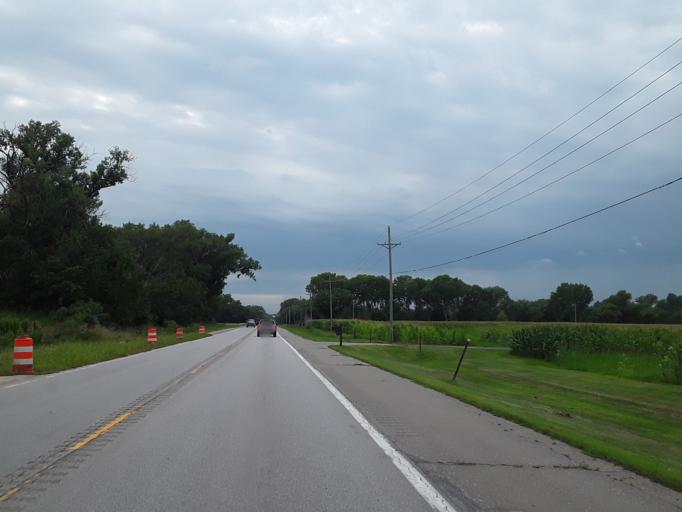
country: US
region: Nebraska
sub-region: Saunders County
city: Yutan
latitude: 41.2338
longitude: -96.3412
